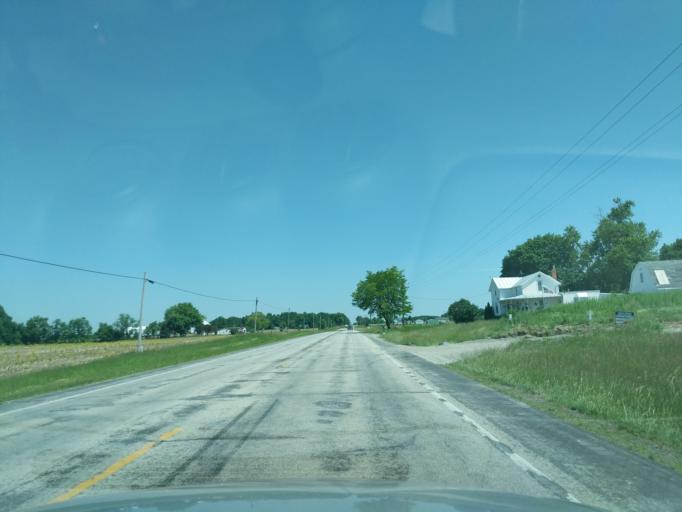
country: US
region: Indiana
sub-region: Whitley County
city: Columbia City
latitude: 41.0935
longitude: -85.4714
